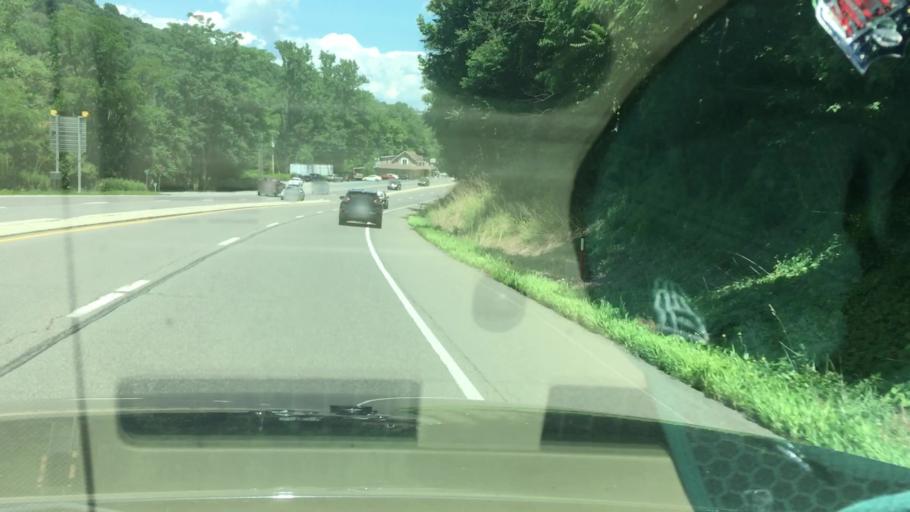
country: US
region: Pennsylvania
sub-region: Berks County
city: West Hamburg
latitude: 40.5910
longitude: -76.0269
